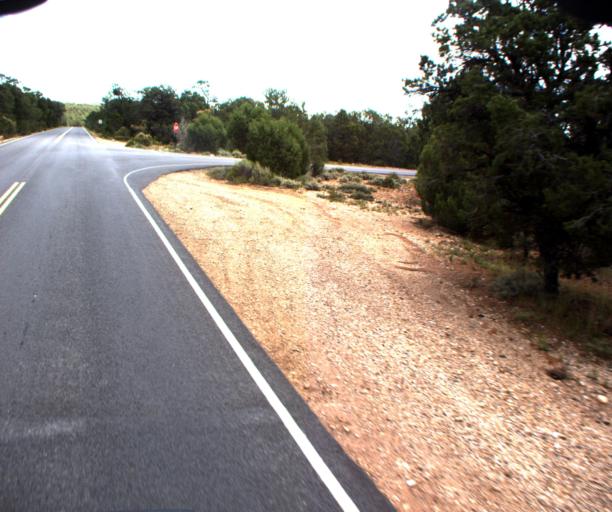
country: US
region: Arizona
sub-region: Coconino County
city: Grand Canyon
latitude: 36.0144
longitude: -111.8693
